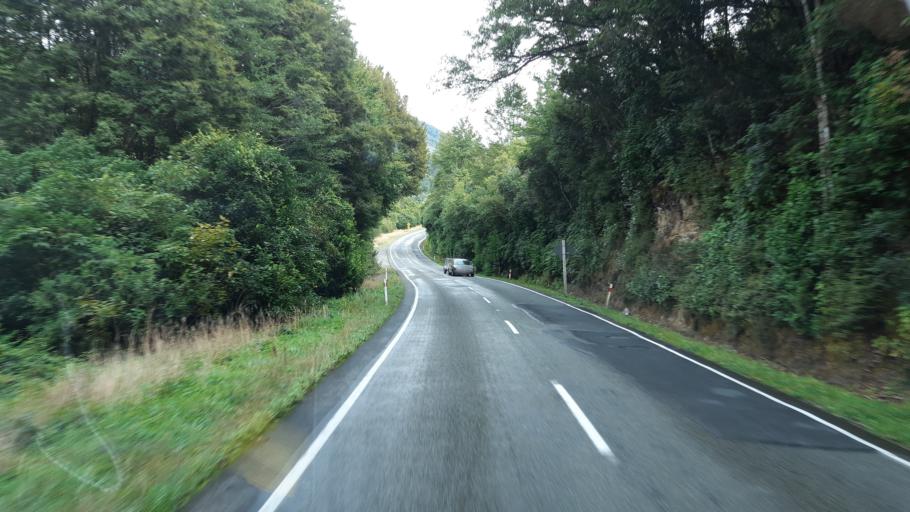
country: NZ
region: West Coast
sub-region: Buller District
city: Westport
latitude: -41.8115
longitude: 172.2289
